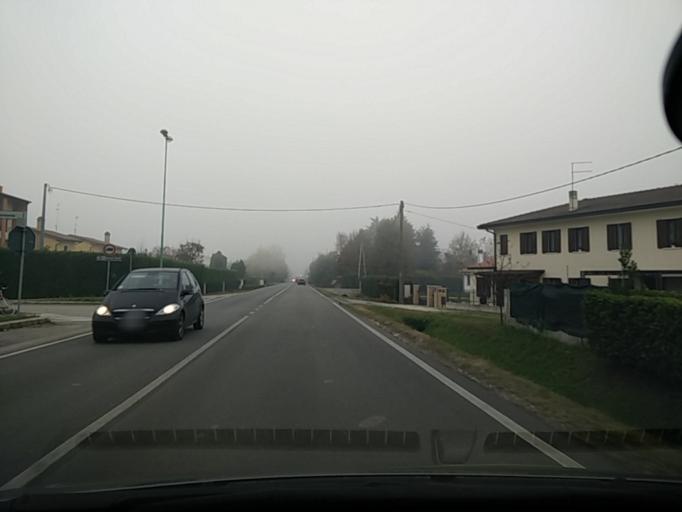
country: IT
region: Veneto
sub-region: Provincia di Venezia
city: Salzano
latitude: 45.5158
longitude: 12.1052
